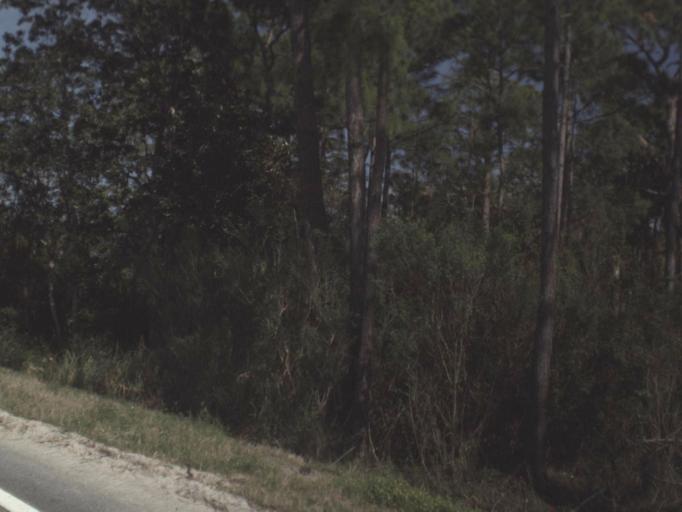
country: US
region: Florida
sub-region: Franklin County
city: Carrabelle
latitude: 29.8335
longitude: -84.6842
